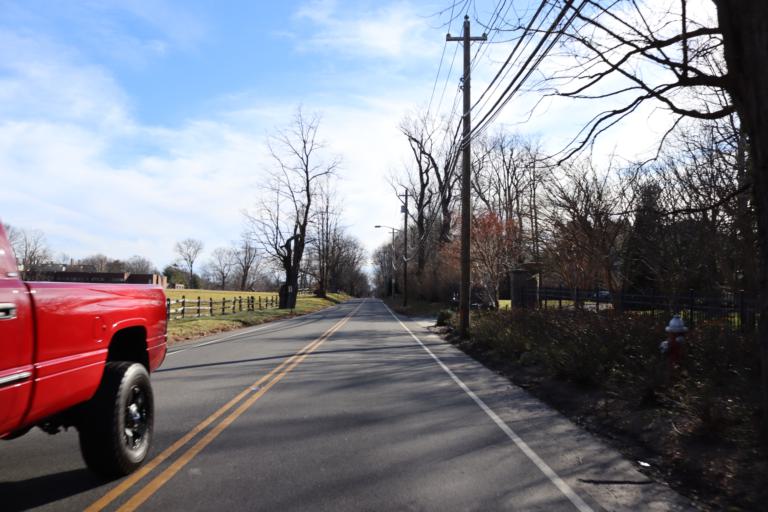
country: US
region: New York
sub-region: Nassau County
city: Glen Cove
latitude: 40.8876
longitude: -73.6315
